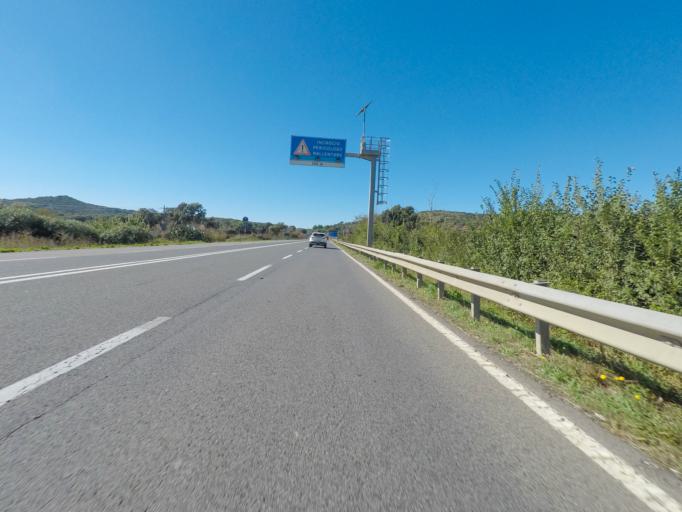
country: IT
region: Tuscany
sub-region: Provincia di Grosseto
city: Orbetello Scalo
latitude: 42.4177
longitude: 11.3067
